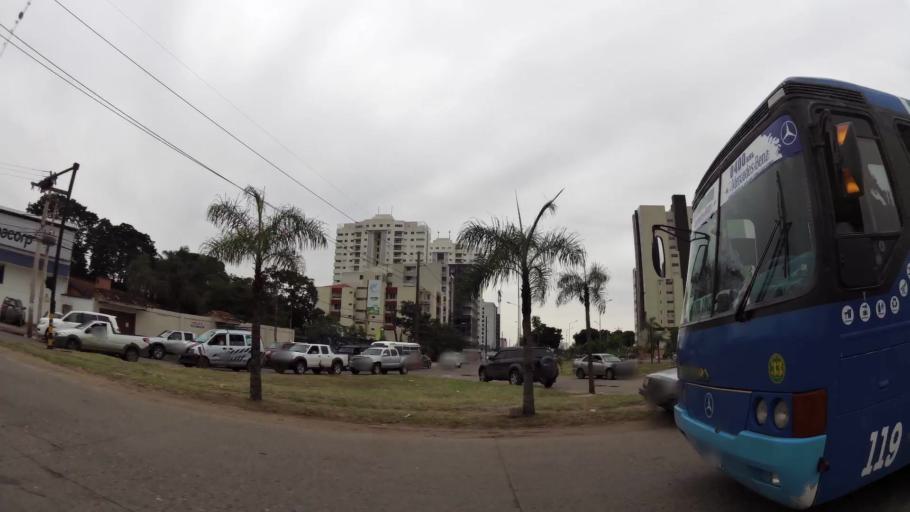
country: BO
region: Santa Cruz
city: Santa Cruz de la Sierra
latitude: -17.7503
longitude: -63.1694
